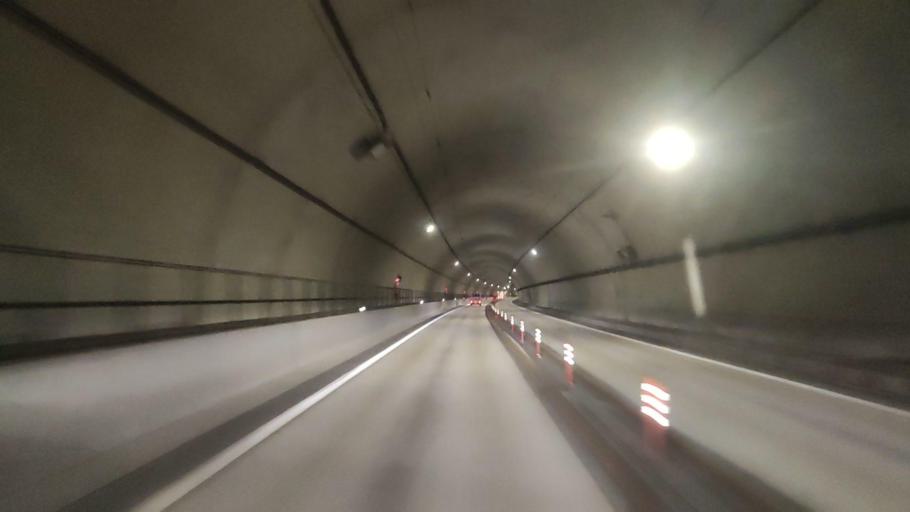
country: JP
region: Wakayama
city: Tanabe
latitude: 33.5911
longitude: 135.4393
